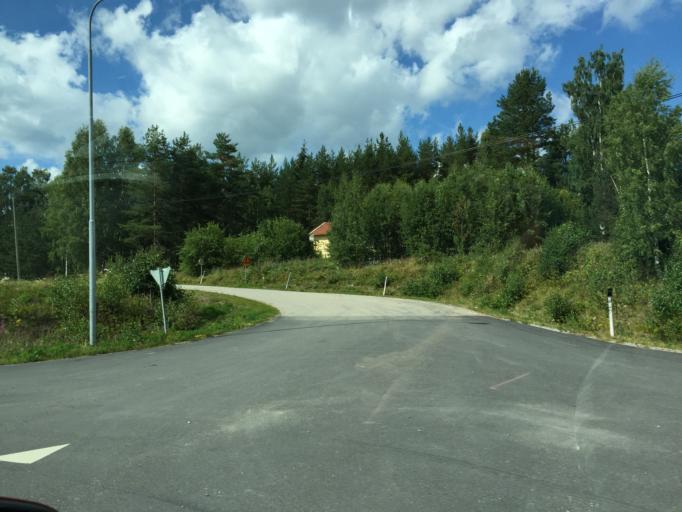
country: SE
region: Gaevleborg
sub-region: Bollnas Kommun
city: Kilafors
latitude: 61.2144
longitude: 16.6417
